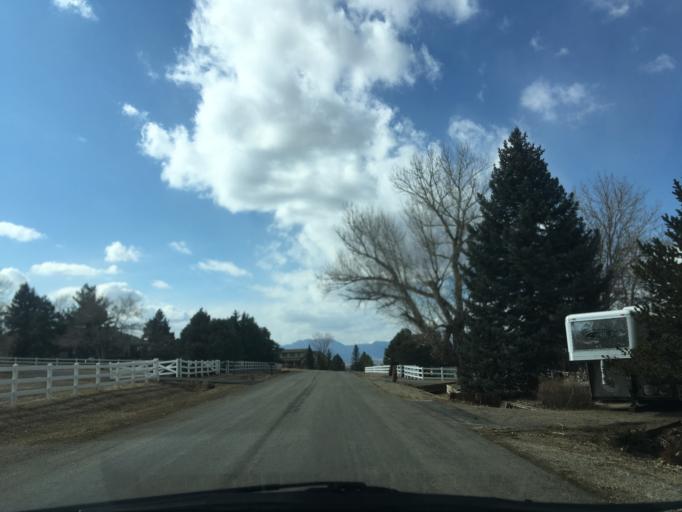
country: US
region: Colorado
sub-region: Boulder County
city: Lafayette
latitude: 39.9600
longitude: -105.0583
